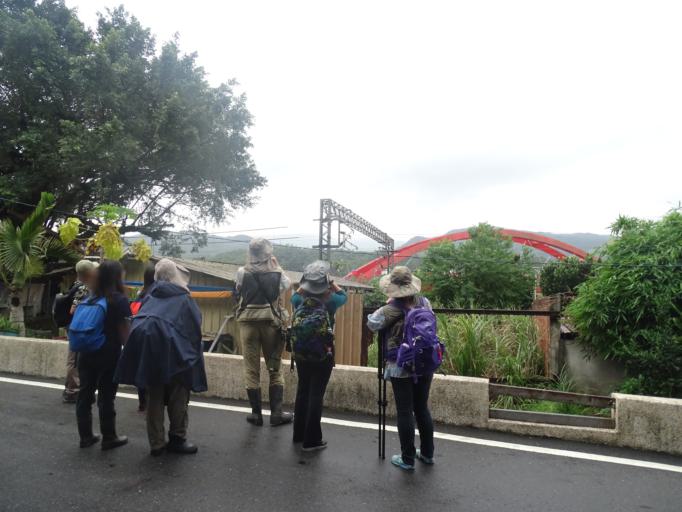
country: TW
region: Taiwan
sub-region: Keelung
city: Keelung
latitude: 25.0221
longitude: 121.9093
